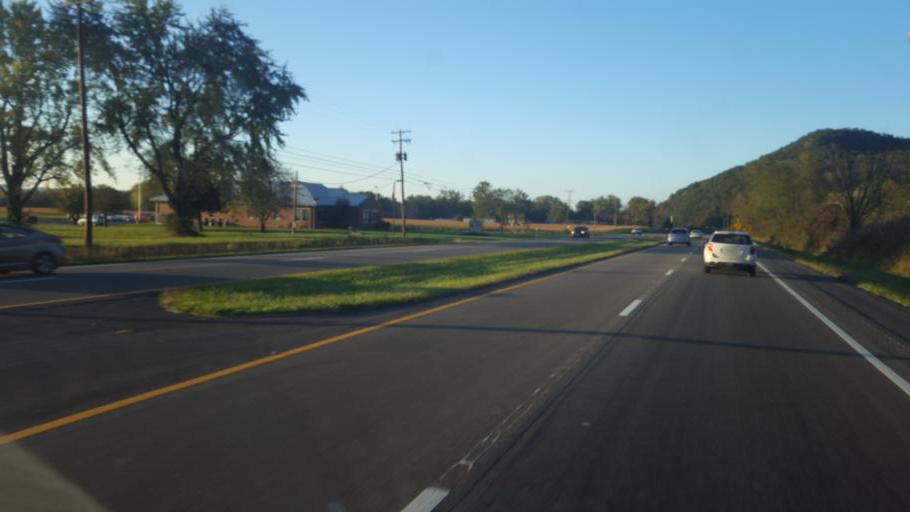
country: US
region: Ohio
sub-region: Scioto County
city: Lucasville
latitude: 38.8366
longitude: -82.9841
